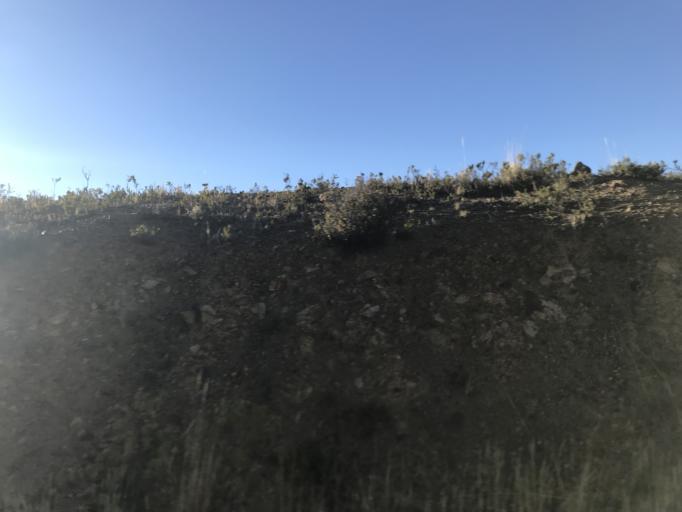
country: BO
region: La Paz
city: San Pablo
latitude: -16.2009
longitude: -68.8317
